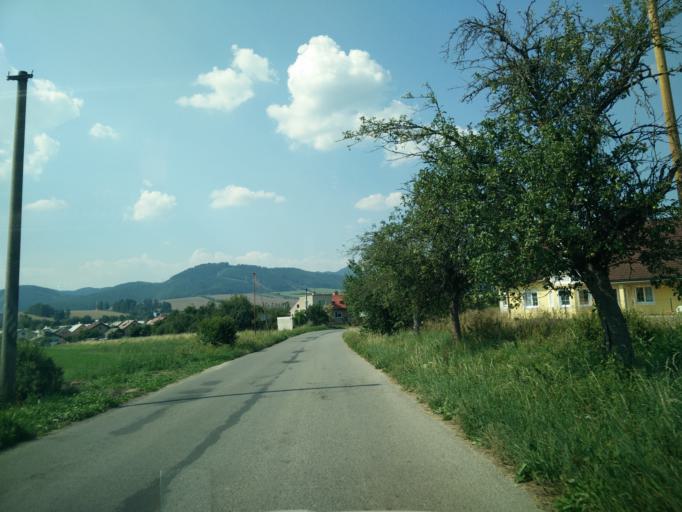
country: SK
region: Zilinsky
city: Rajec
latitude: 49.0794
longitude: 18.6416
